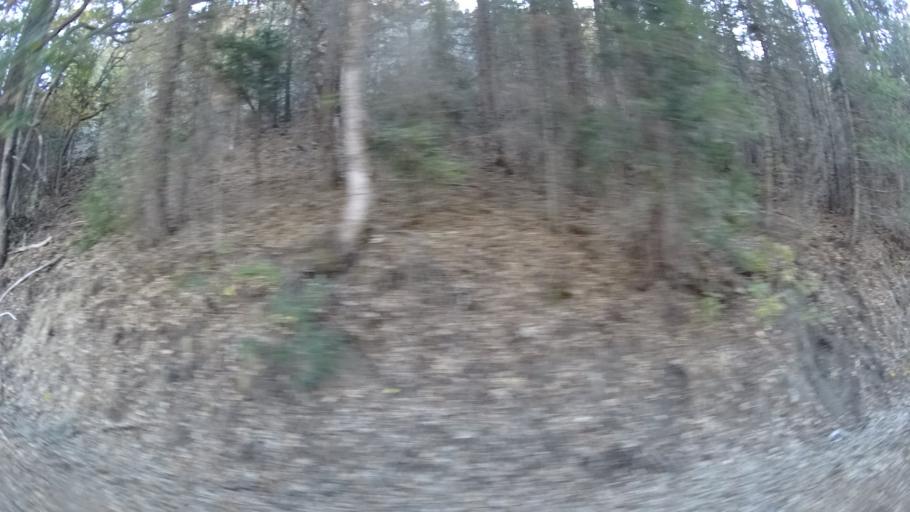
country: US
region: California
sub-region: Siskiyou County
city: Yreka
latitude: 41.8323
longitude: -122.9483
